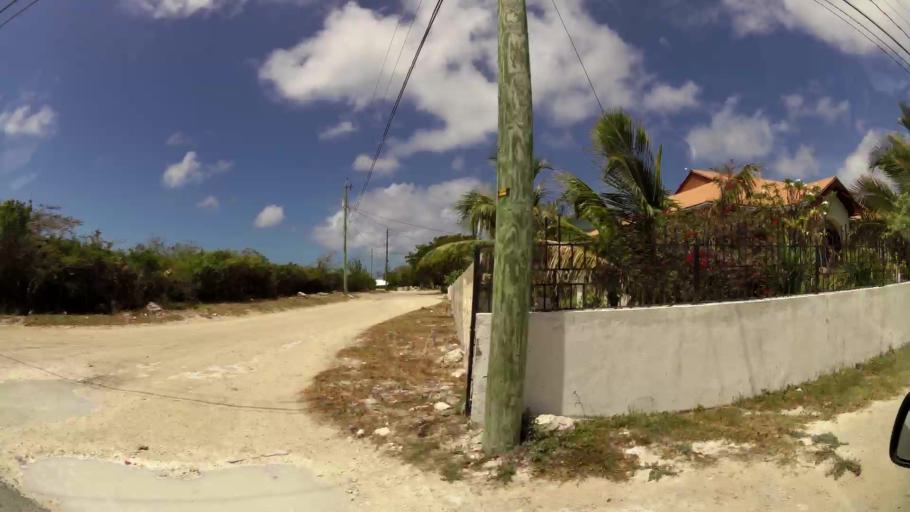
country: TC
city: Cockburn Town
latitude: 21.4559
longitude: -71.1427
